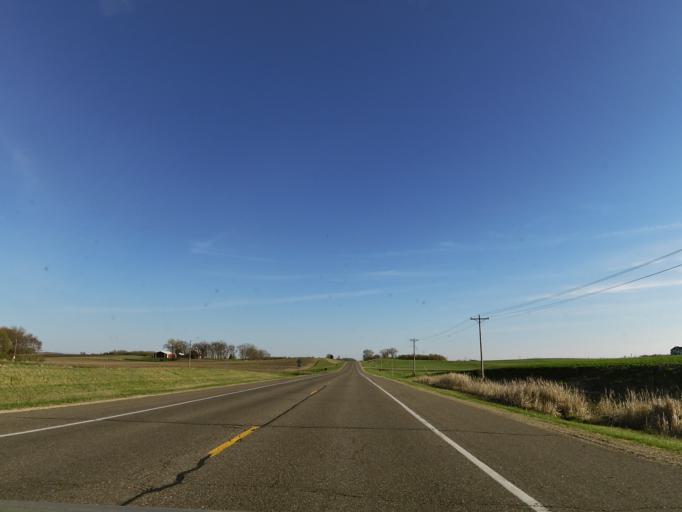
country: US
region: Minnesota
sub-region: Dakota County
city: Lakeville
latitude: 44.5562
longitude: -93.2076
